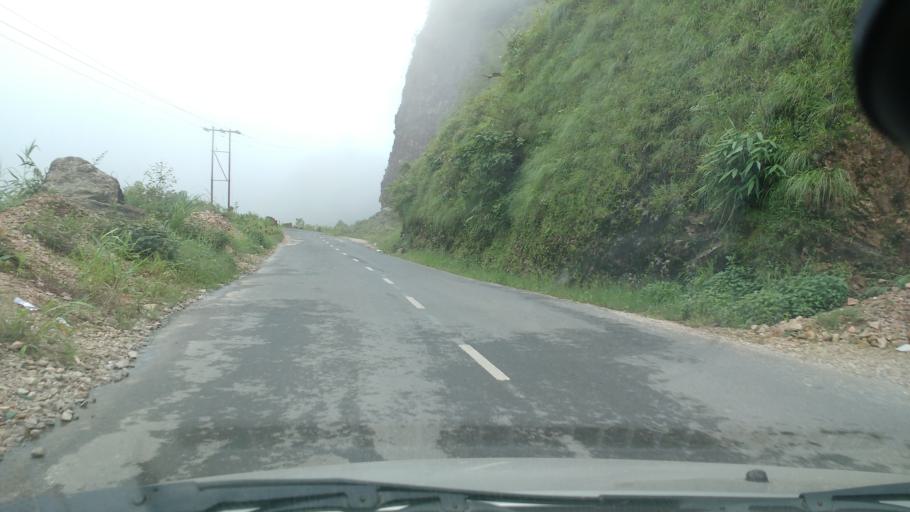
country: IN
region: Meghalaya
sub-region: East Khasi Hills
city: Cherrapunji
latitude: 25.3716
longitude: 91.8765
